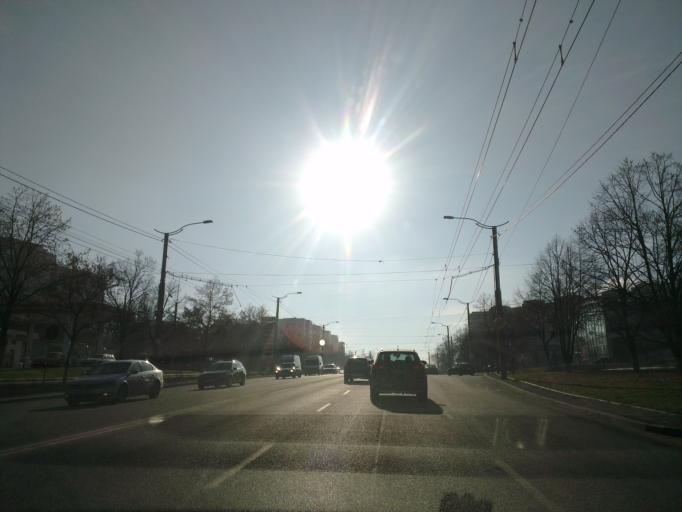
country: MD
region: Chisinau
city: Chisinau
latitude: 47.0402
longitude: 28.8801
